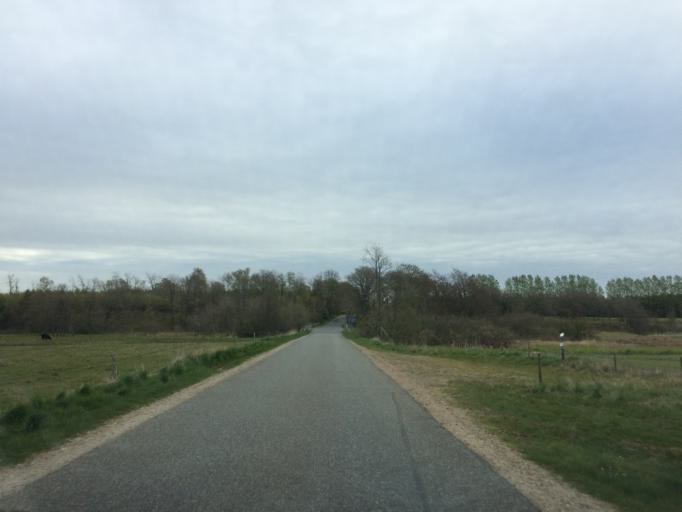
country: DK
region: Central Jutland
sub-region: Viborg Kommune
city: Karup
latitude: 56.3467
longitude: 9.1040
